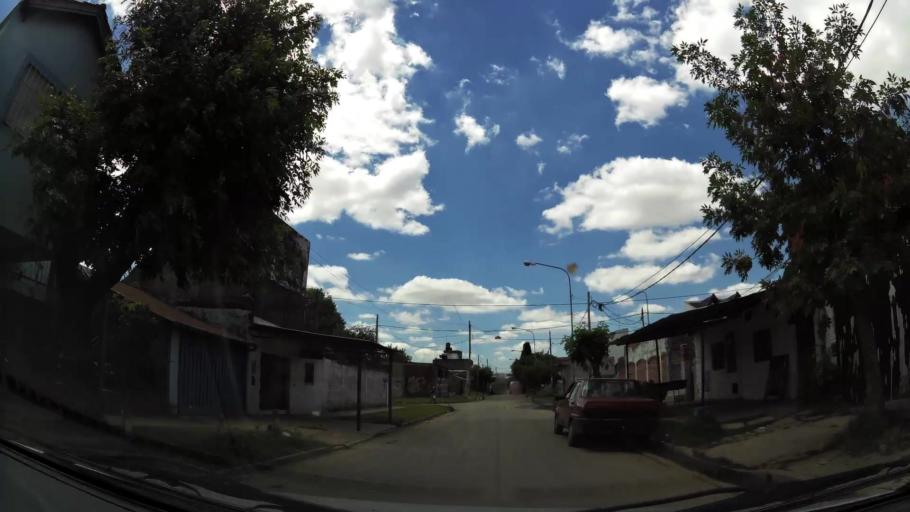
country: AR
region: Buenos Aires
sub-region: Partido de Lanus
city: Lanus
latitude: -34.7211
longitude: -58.4213
